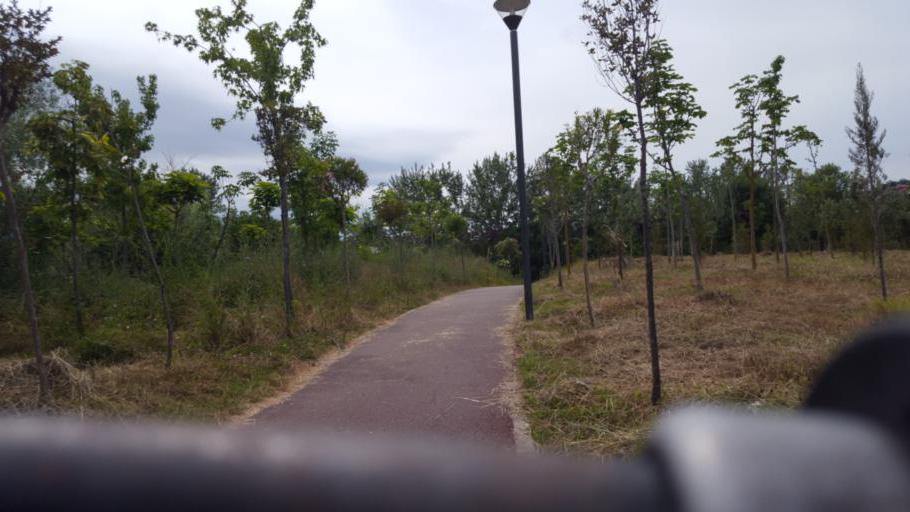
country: AL
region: Tirane
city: Tirana
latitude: 41.3064
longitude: 19.8216
